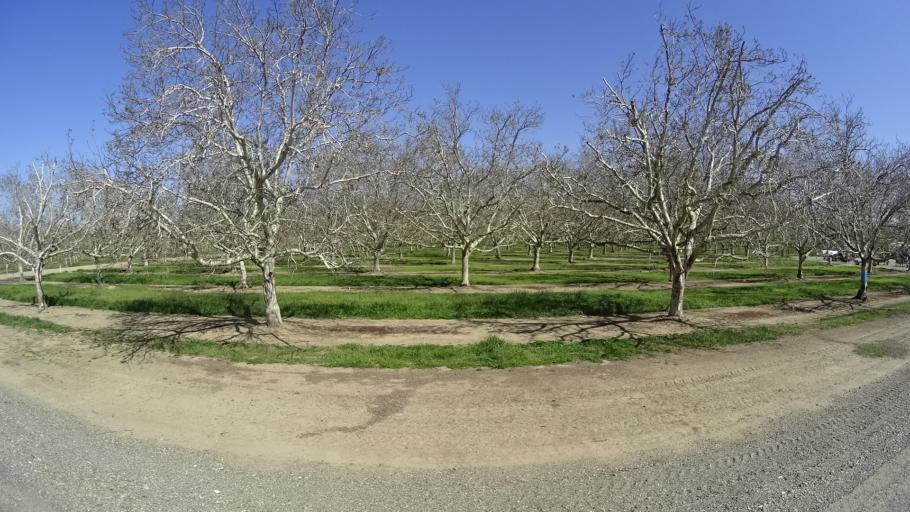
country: US
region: California
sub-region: Glenn County
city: Willows
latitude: 39.4501
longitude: -122.0215
